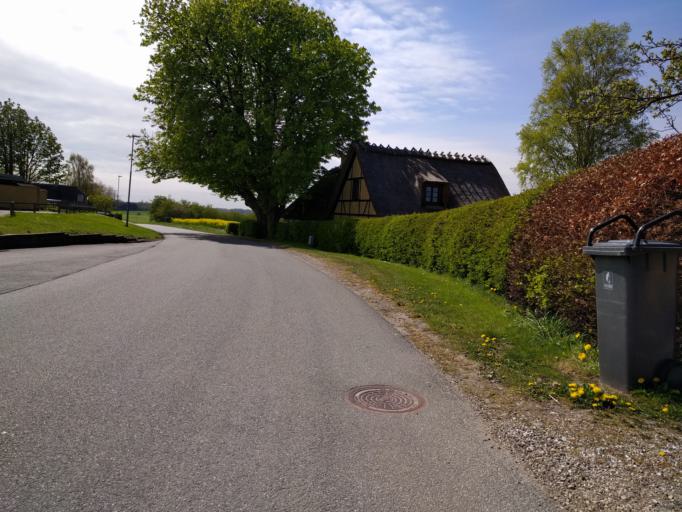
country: DK
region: South Denmark
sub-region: Kerteminde Kommune
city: Langeskov
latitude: 55.4110
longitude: 10.5943
